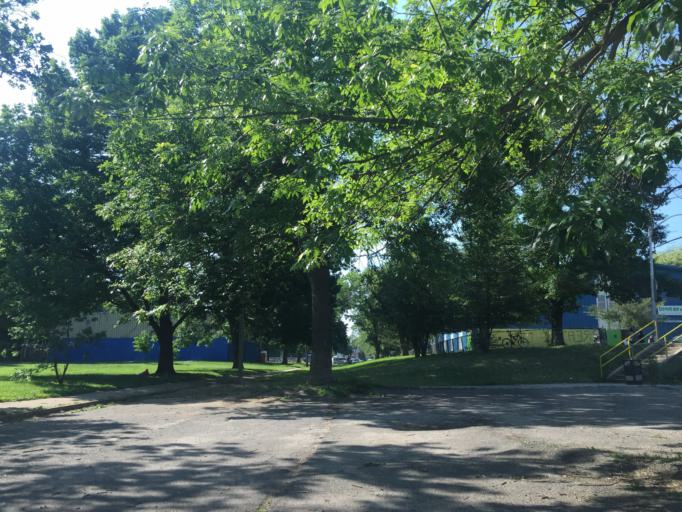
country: US
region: Maryland
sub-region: Baltimore County
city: Lochearn
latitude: 39.3331
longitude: -76.6649
